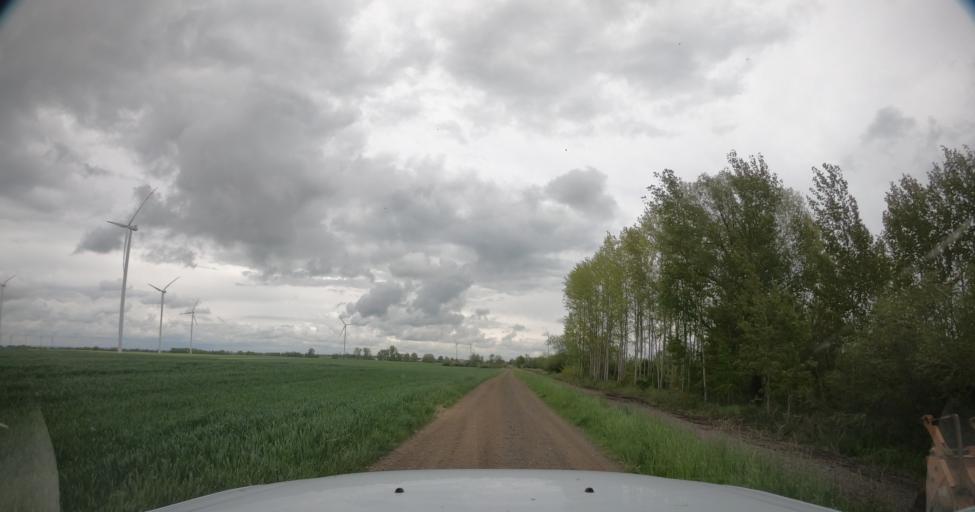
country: PL
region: West Pomeranian Voivodeship
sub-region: Powiat pyrzycki
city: Kozielice
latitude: 53.1039
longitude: 14.8061
